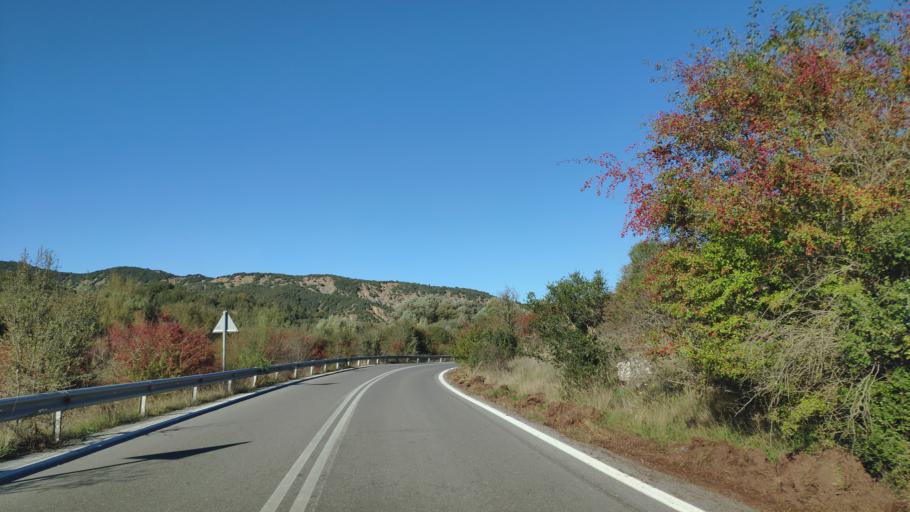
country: GR
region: Peloponnese
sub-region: Nomos Arkadias
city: Dimitsana
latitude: 37.6264
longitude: 22.0616
